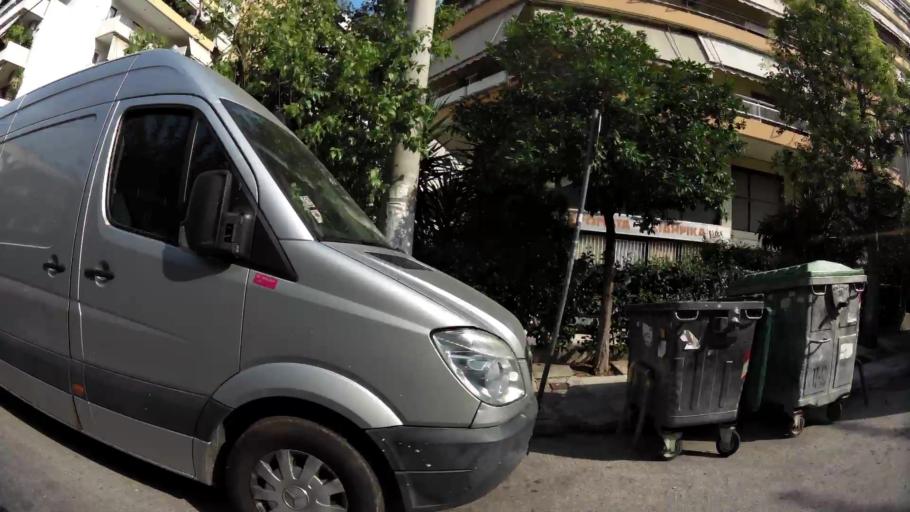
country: GR
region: Attica
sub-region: Nomarchia Athinas
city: Galatsi
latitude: 38.0125
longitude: 23.7473
